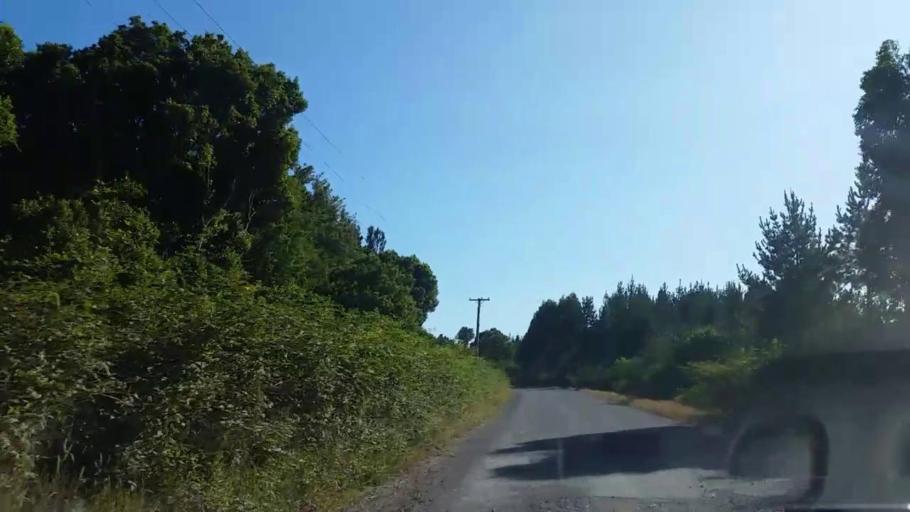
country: NZ
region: Bay of Plenty
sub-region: Kawerau District
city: Kawerau
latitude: -38.0106
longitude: 176.4910
